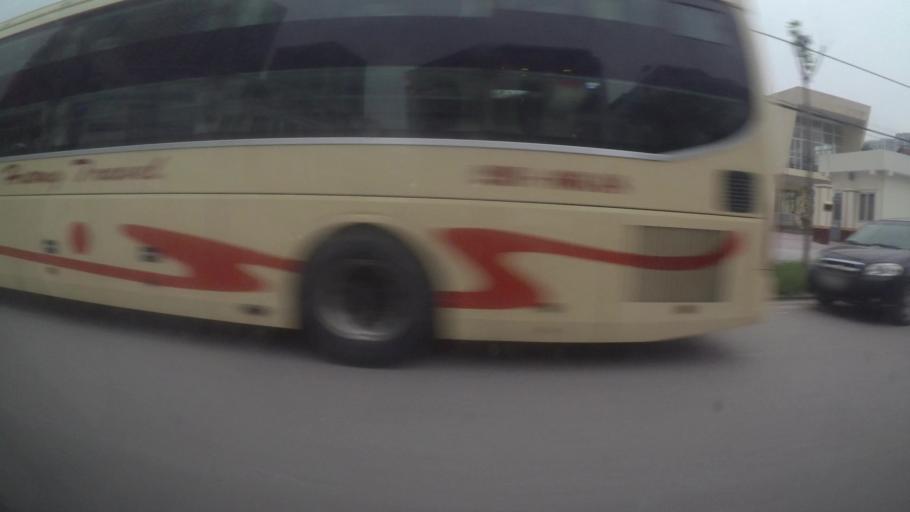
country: VN
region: Ha Noi
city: Cau Dien
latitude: 21.0372
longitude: 105.7597
